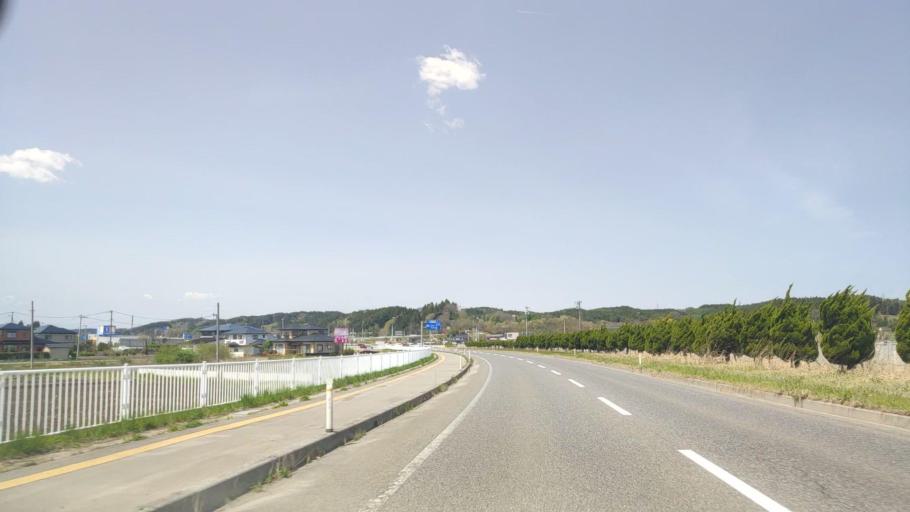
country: JP
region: Aomori
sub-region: Hachinohe Shi
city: Uchimaru
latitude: 40.5169
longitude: 141.4341
